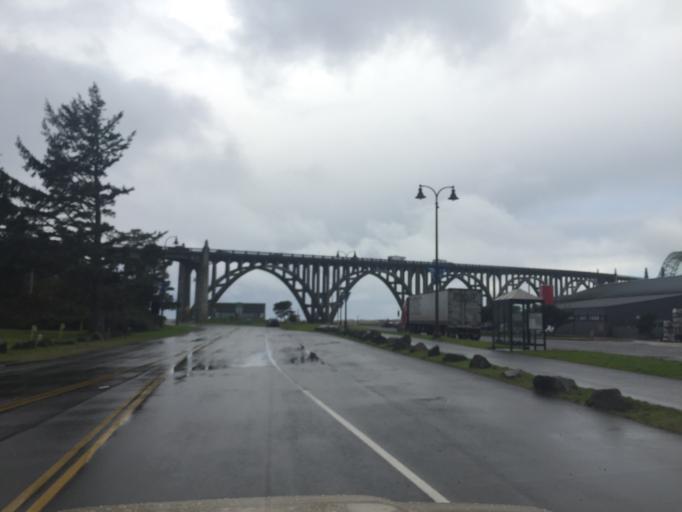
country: US
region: Oregon
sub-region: Lincoln County
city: Newport
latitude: 44.6194
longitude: -124.0508
